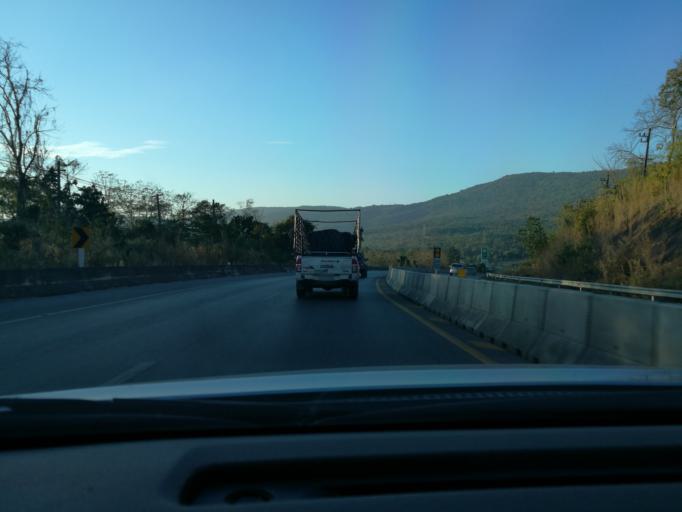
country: TH
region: Phitsanulok
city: Wang Thong
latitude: 16.8583
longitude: 100.5048
